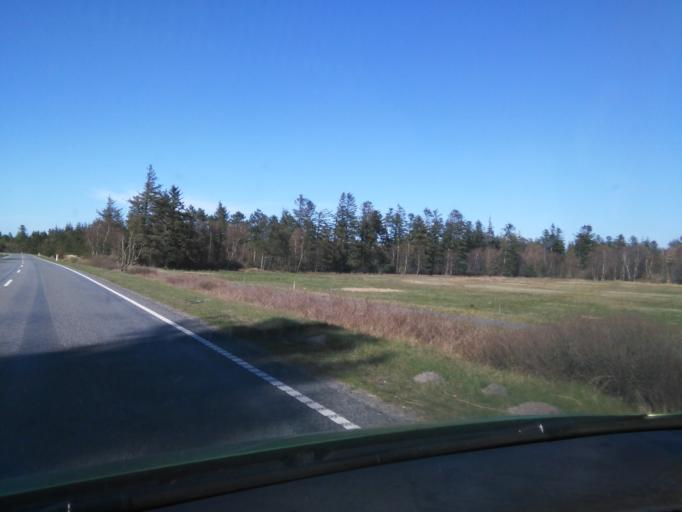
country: DK
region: South Denmark
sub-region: Varde Kommune
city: Oksbol
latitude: 55.5822
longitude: 8.2298
